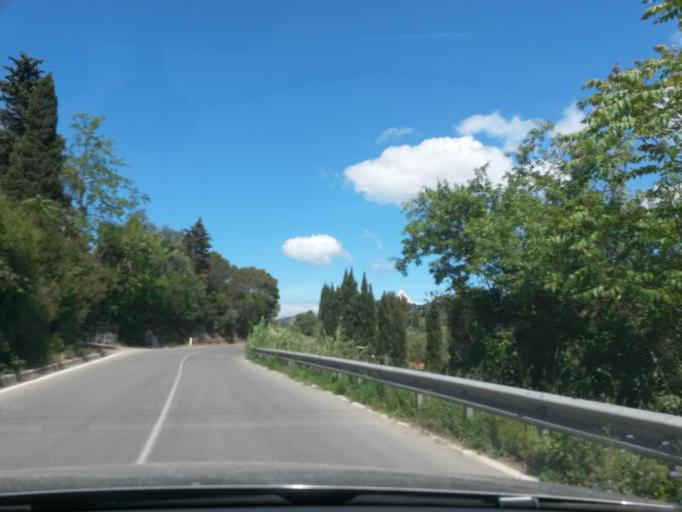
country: IT
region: Tuscany
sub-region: Provincia di Livorno
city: Capoliveri
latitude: 42.7703
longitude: 10.3436
